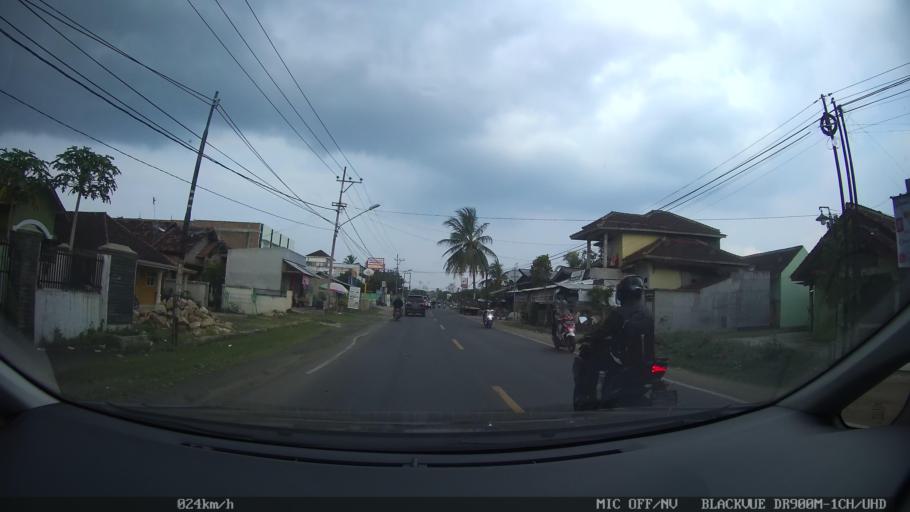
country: ID
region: Lampung
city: Gedongtataan
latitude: -5.3752
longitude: 105.0854
